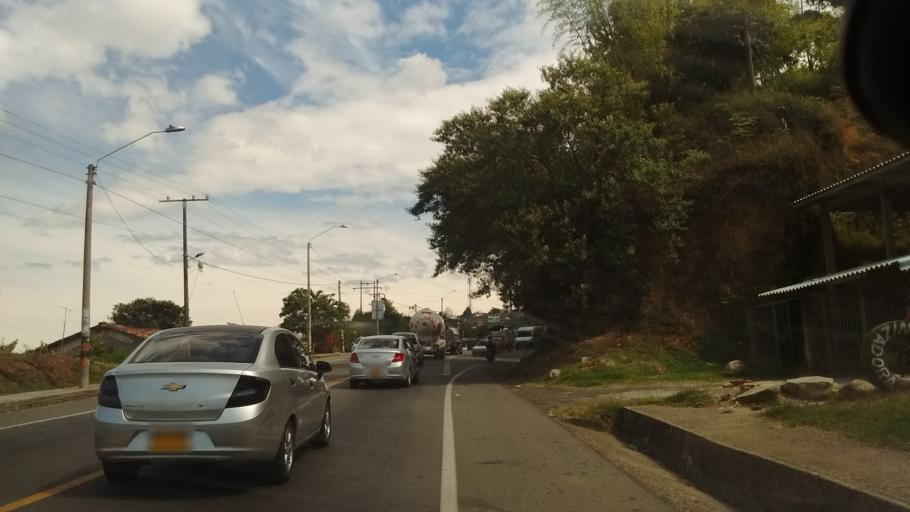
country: CO
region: Cauca
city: Cajibio
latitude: 2.6337
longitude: -76.5278
